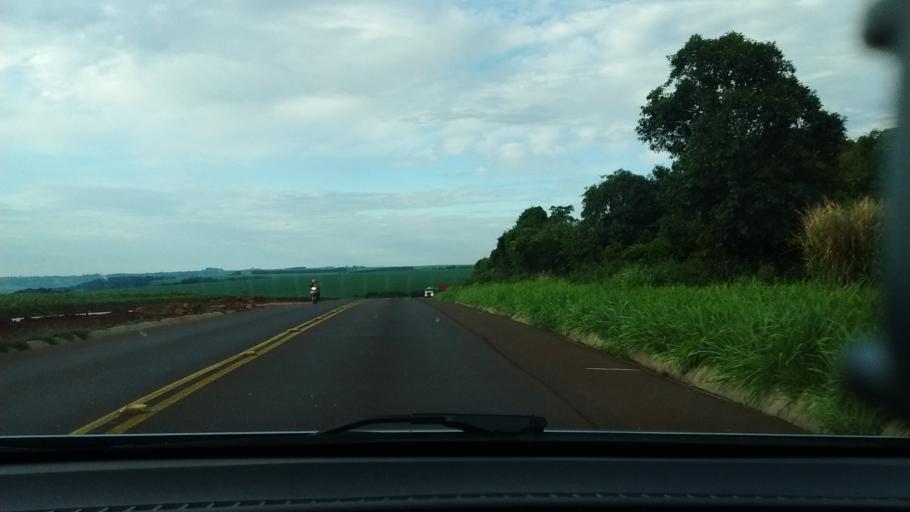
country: BR
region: Parana
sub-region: Cascavel
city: Cascavel
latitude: -25.0592
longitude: -53.5623
